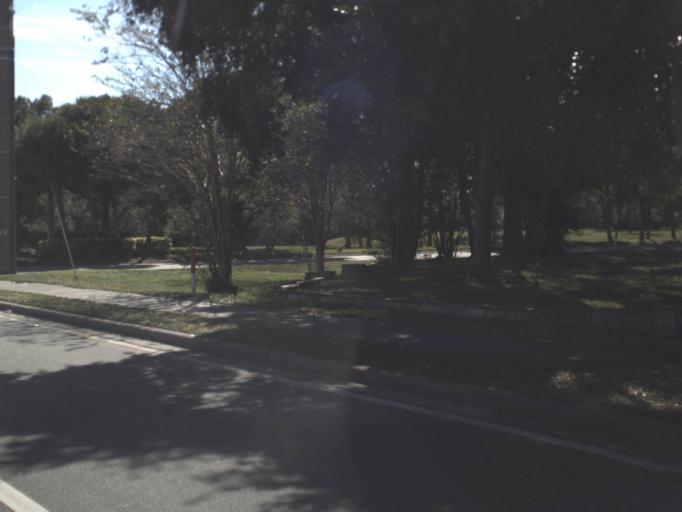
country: US
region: Florida
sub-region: Brevard County
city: South Patrick Shores
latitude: 28.2255
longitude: -80.6780
